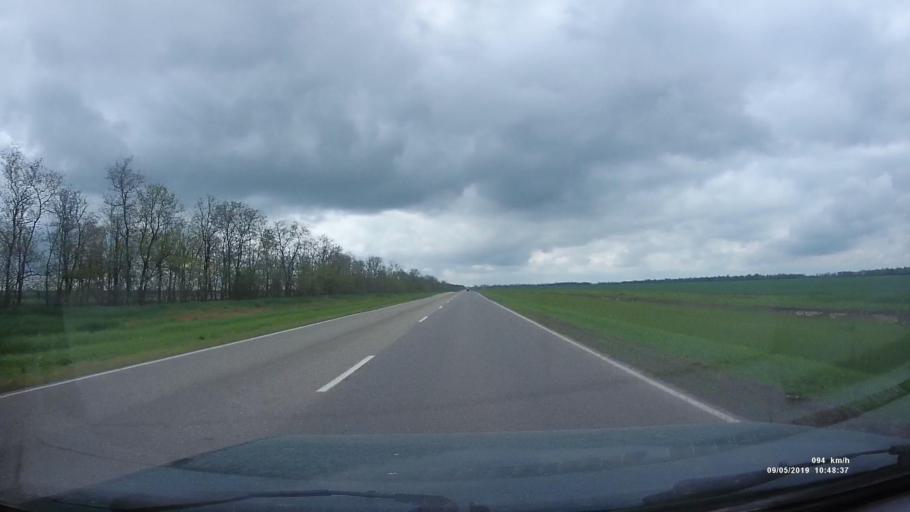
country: RU
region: Rostov
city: Peshkovo
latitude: 46.9542
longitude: 39.3556
